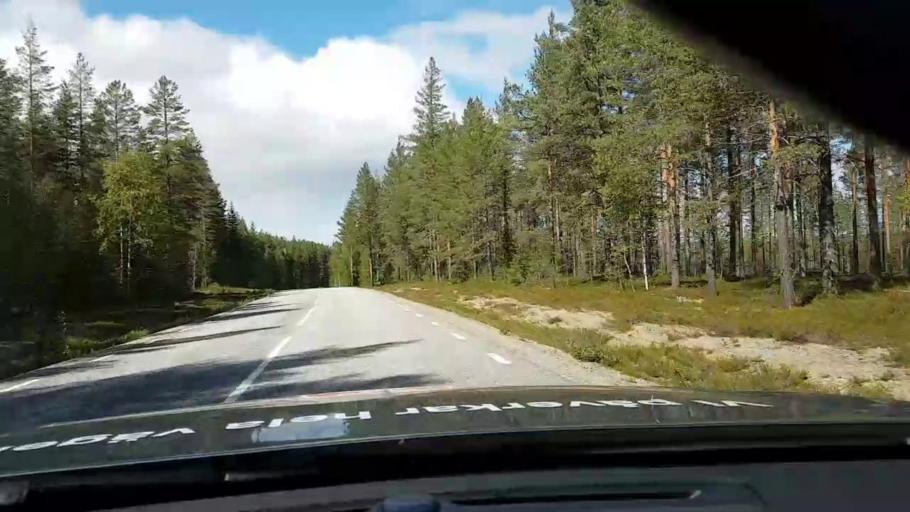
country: SE
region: Vaesternorrland
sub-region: OErnskoeldsviks Kommun
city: Bredbyn
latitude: 63.6661
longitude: 17.8331
